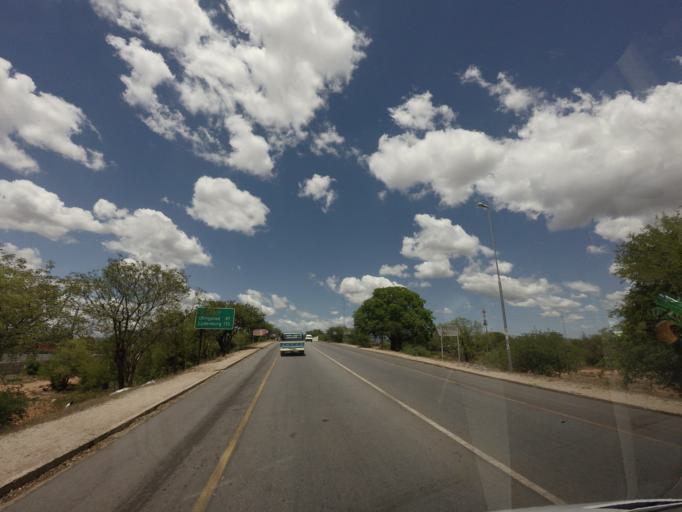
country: ZA
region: Limpopo
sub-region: Mopani District Municipality
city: Hoedspruit
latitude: -24.3496
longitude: 30.9538
